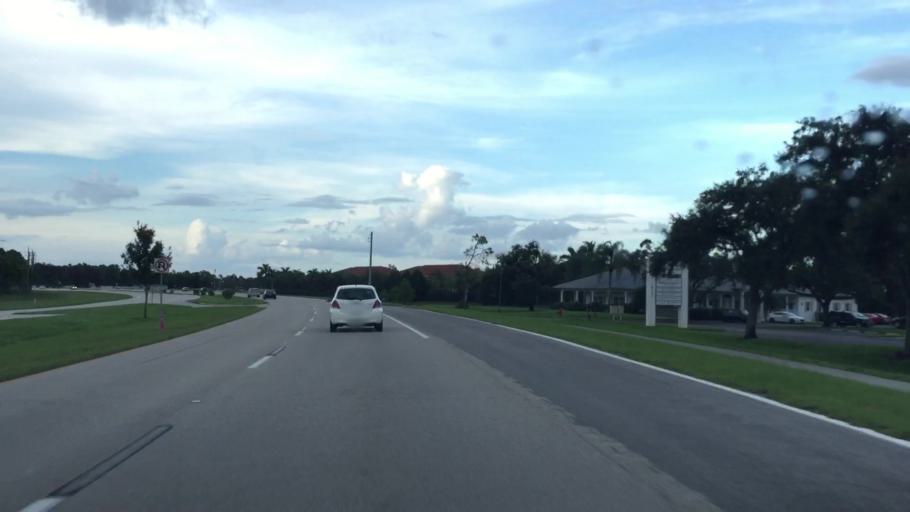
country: US
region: Florida
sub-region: Lee County
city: Fort Myers
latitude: 26.5949
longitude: -81.8127
